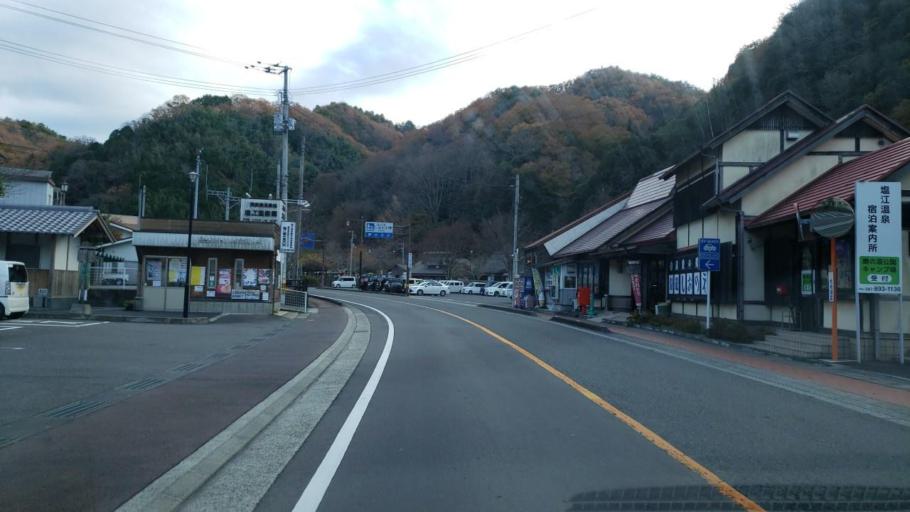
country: JP
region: Tokushima
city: Wakimachi
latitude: 34.1705
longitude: 134.0821
